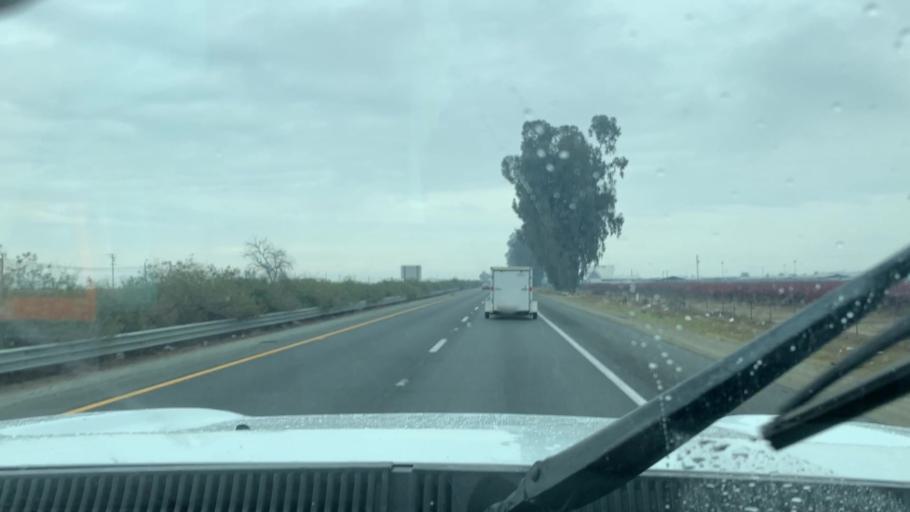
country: US
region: California
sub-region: Kern County
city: Delano
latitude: 35.8103
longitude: -119.2569
